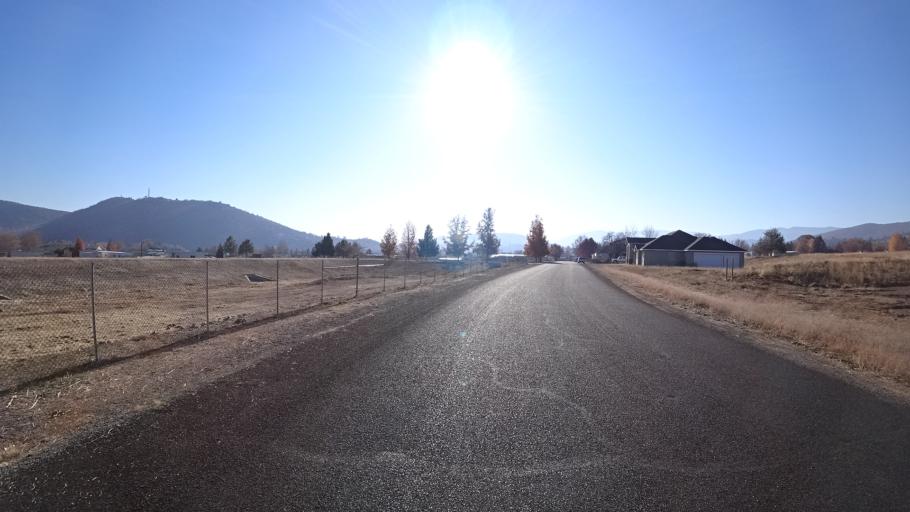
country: US
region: California
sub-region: Siskiyou County
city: Yreka
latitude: 41.7268
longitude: -122.6465
